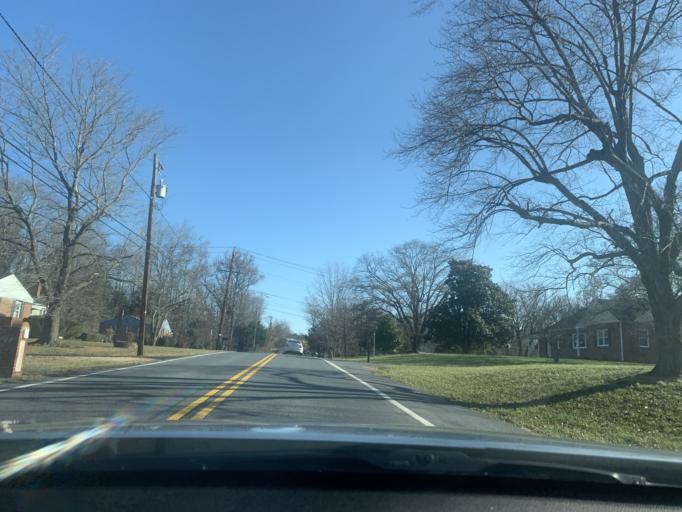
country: US
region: Maryland
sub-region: Prince George's County
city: Camp Springs
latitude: 38.8175
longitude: -76.9223
